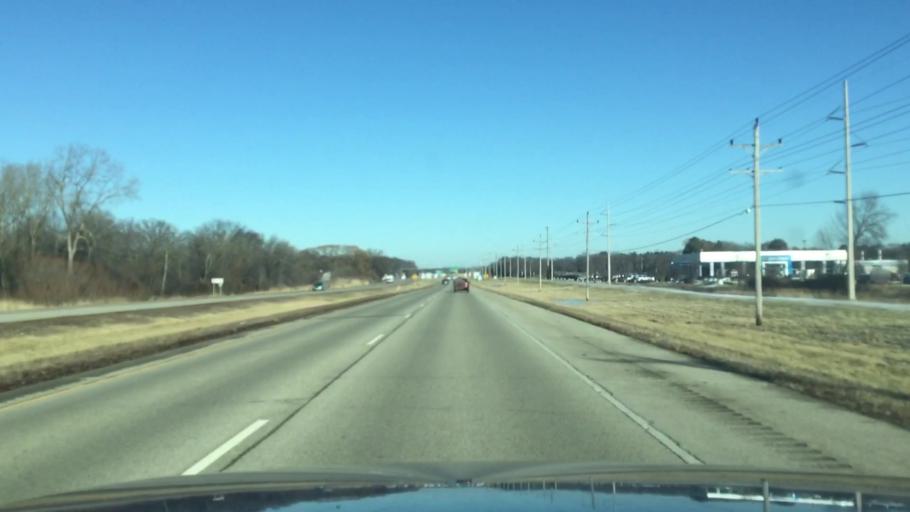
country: US
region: Wisconsin
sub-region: Racine County
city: Browns Lake
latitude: 42.7065
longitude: -88.2439
